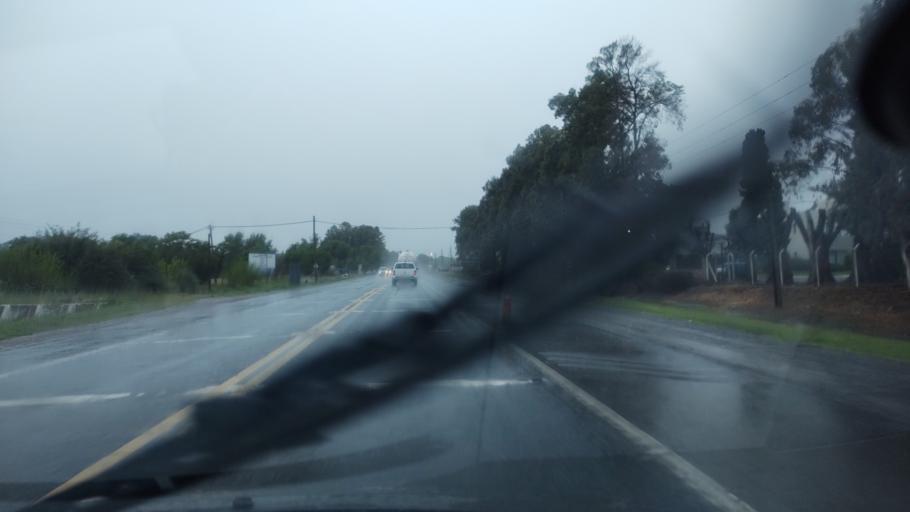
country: AR
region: Buenos Aires
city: Canuelas
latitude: -35.0391
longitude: -58.7599
